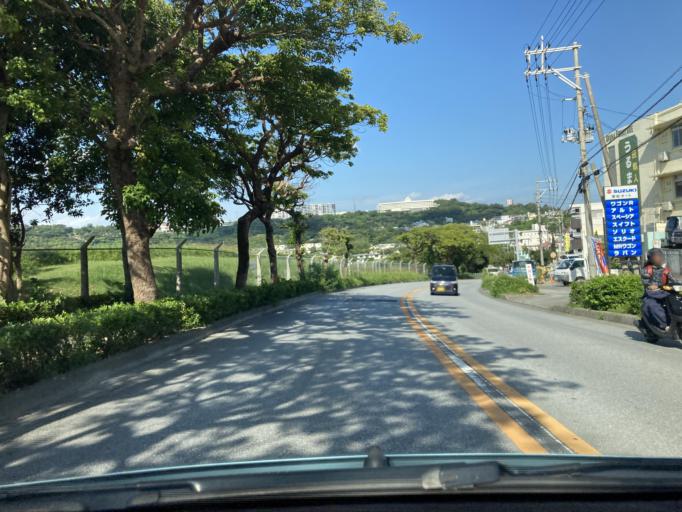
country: JP
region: Okinawa
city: Chatan
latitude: 26.2987
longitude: 127.7875
